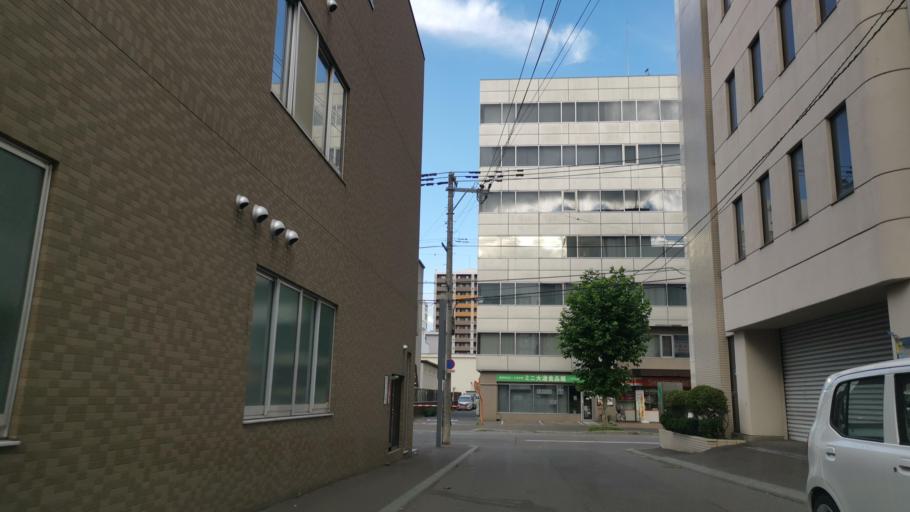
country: JP
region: Hokkaido
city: Sapporo
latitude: 43.0634
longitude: 141.3299
